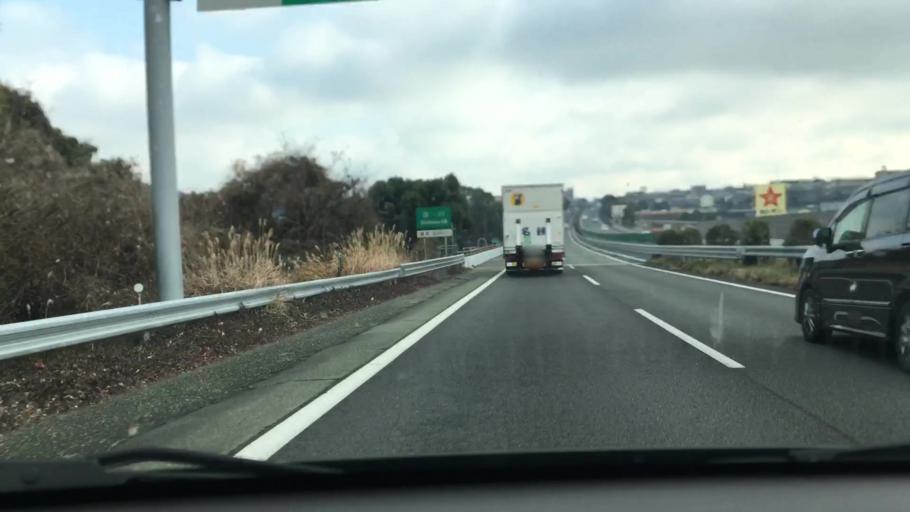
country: JP
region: Kumamoto
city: Kumamoto
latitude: 32.8446
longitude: 130.7716
